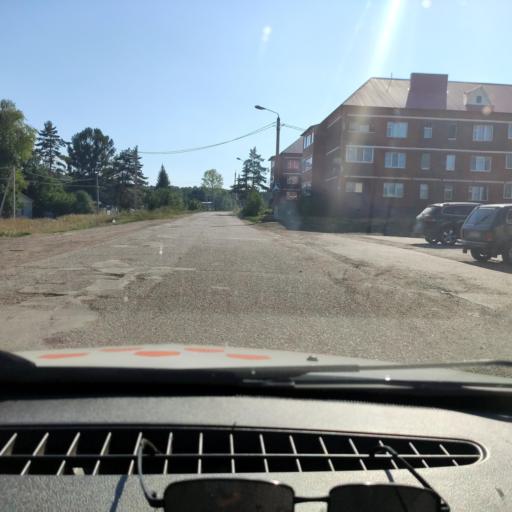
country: RU
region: Bashkortostan
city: Tolbazy
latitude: 54.0057
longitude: 55.8904
